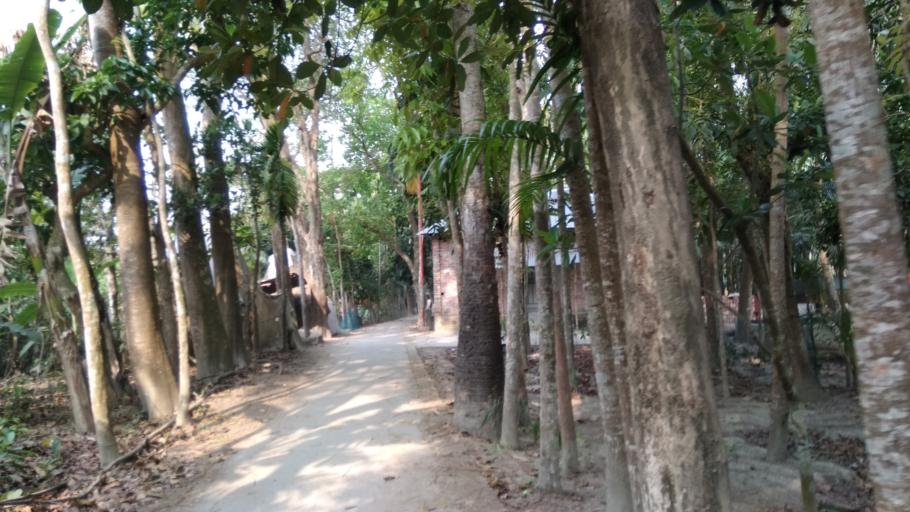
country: BD
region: Barisal
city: Mehendiganj
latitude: 22.9500
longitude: 90.4141
